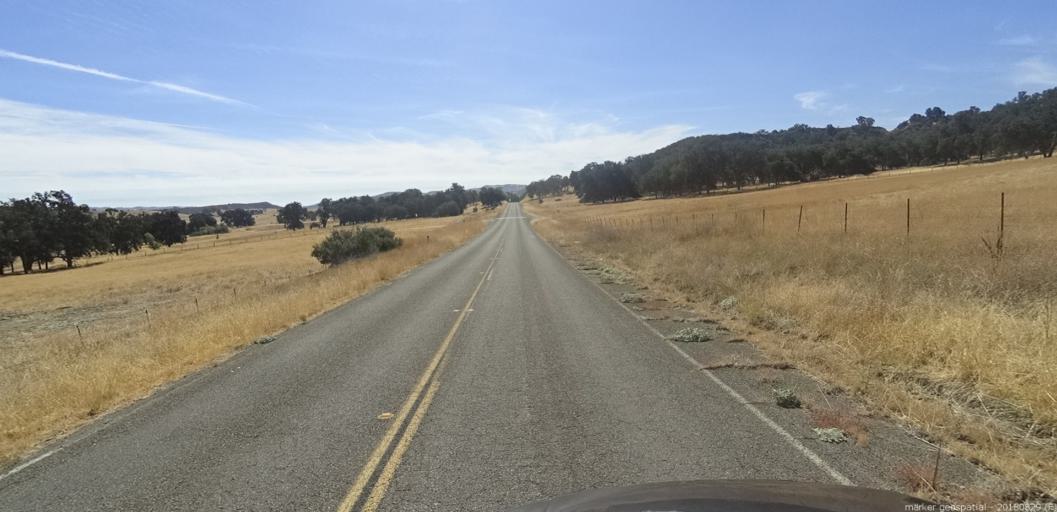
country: US
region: California
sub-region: San Luis Obispo County
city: Lake Nacimiento
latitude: 35.8241
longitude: -121.0144
